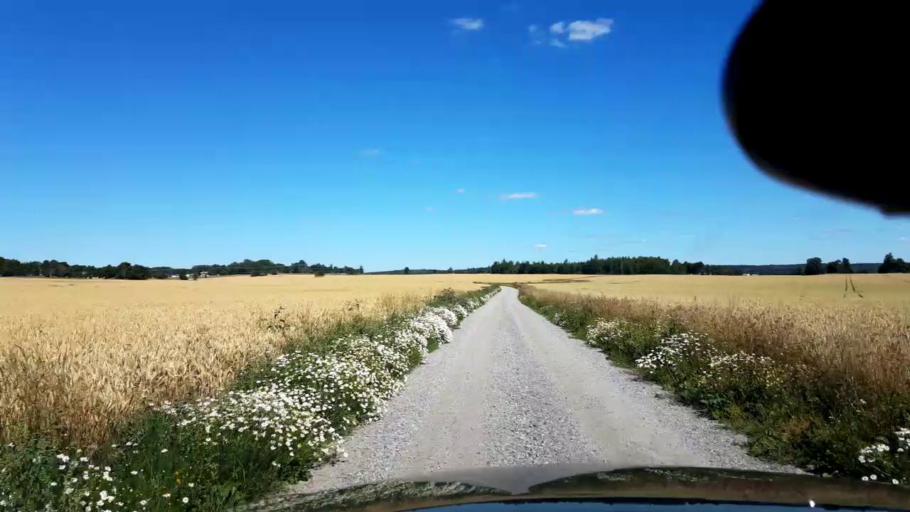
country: SE
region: Stockholm
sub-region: Upplands-Bro Kommun
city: Bro
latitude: 59.5872
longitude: 17.6370
